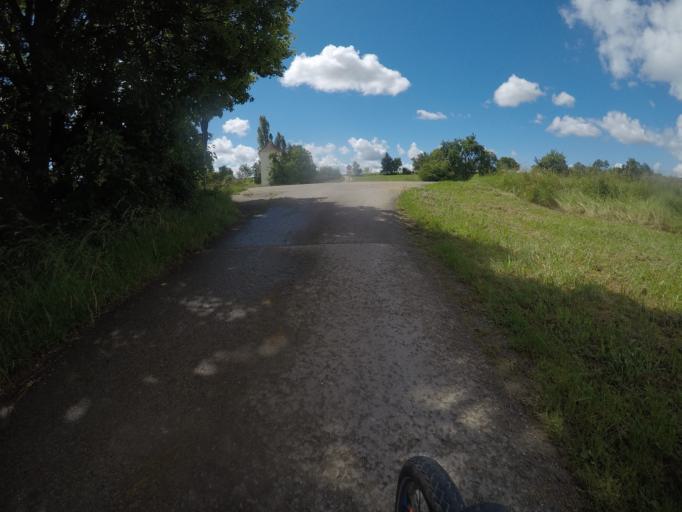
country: DE
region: Baden-Wuerttemberg
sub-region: Regierungsbezirk Stuttgart
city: Motzingen
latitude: 48.4973
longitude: 8.7495
